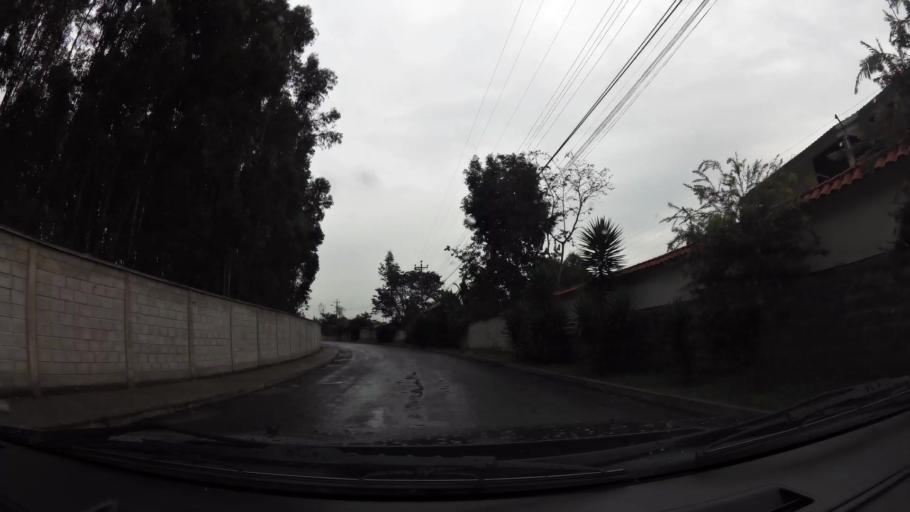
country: EC
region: Pichincha
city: Sangolqui
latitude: -0.2838
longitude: -78.4481
